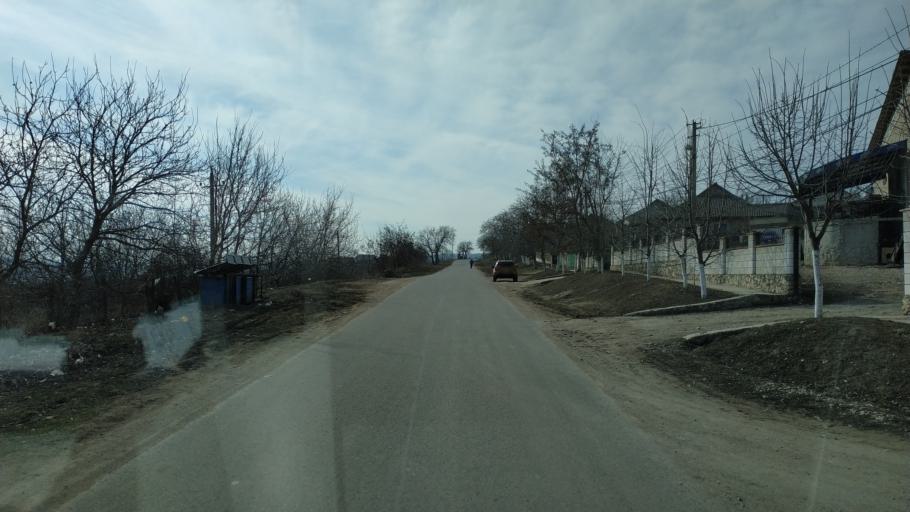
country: MD
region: Nisporeni
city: Nisporeni
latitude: 47.1524
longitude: 28.1295
